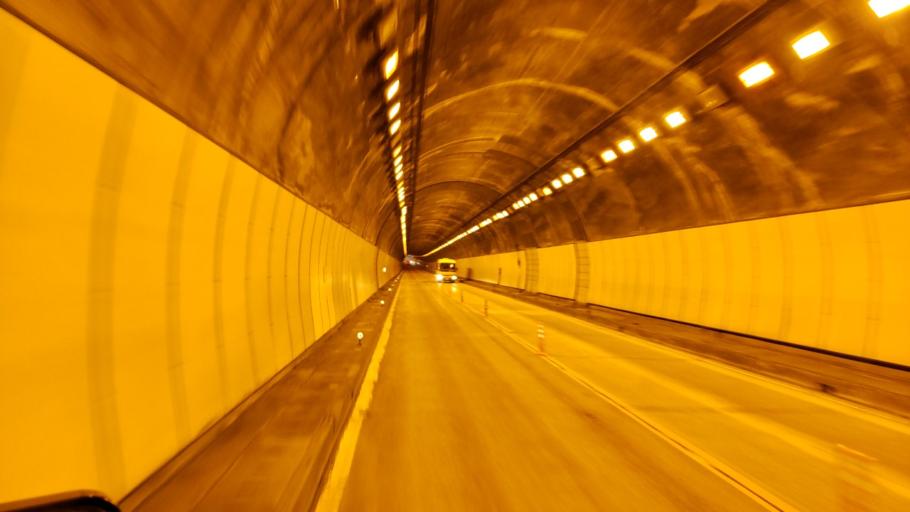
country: JP
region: Hyogo
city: Himeji
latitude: 34.9703
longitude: 134.7690
